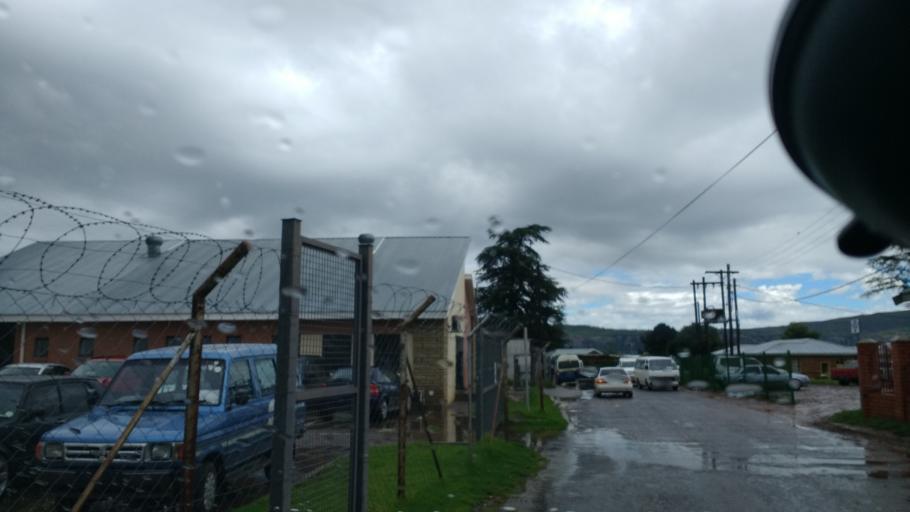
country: LS
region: Maseru
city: Nako
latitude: -29.4616
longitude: 27.7347
